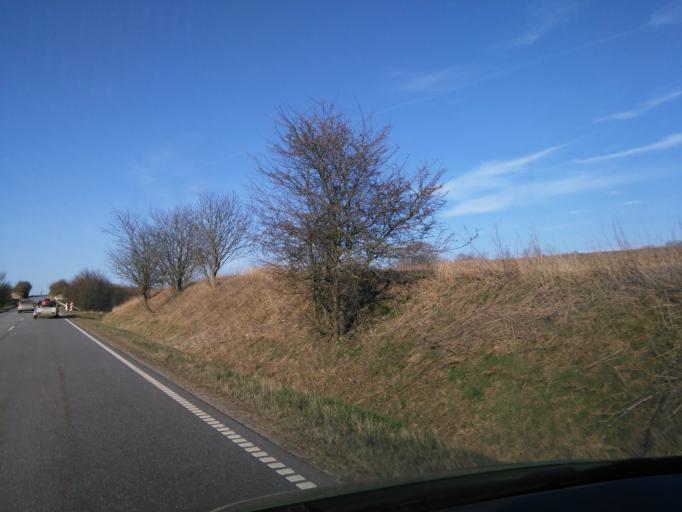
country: DK
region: Central Jutland
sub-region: Skanderborg Kommune
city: Ry
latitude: 55.9805
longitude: 9.7612
